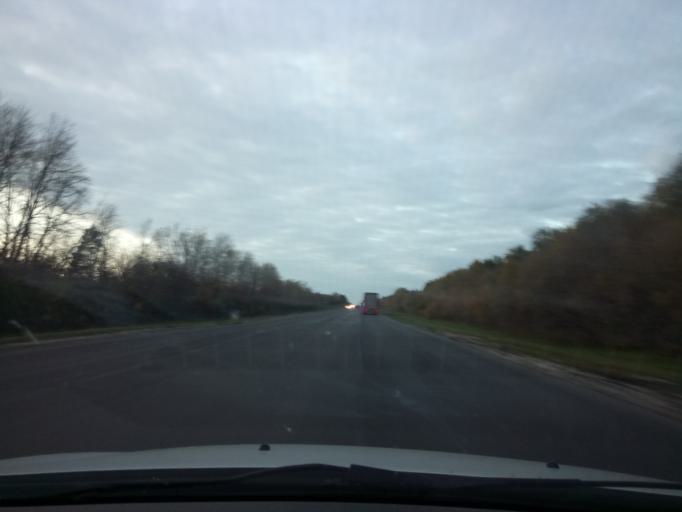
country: RU
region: Nizjnij Novgorod
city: Bol'shoye Murashkino
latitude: 55.8042
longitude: 44.7633
